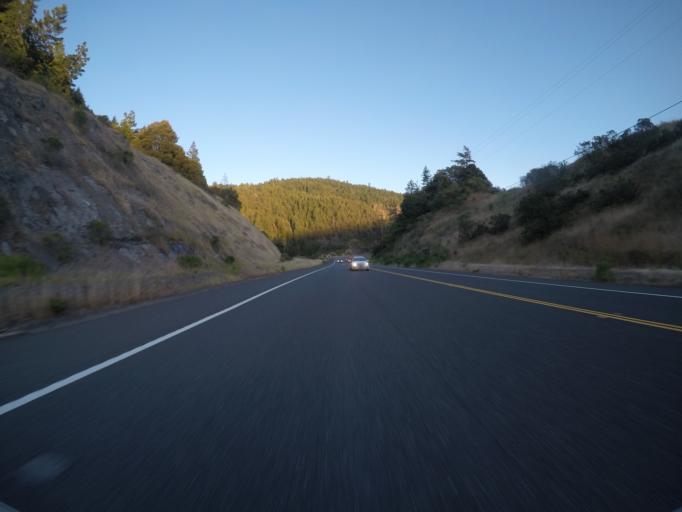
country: US
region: California
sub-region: Humboldt County
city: Redway
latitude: 39.9304
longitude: -123.7630
